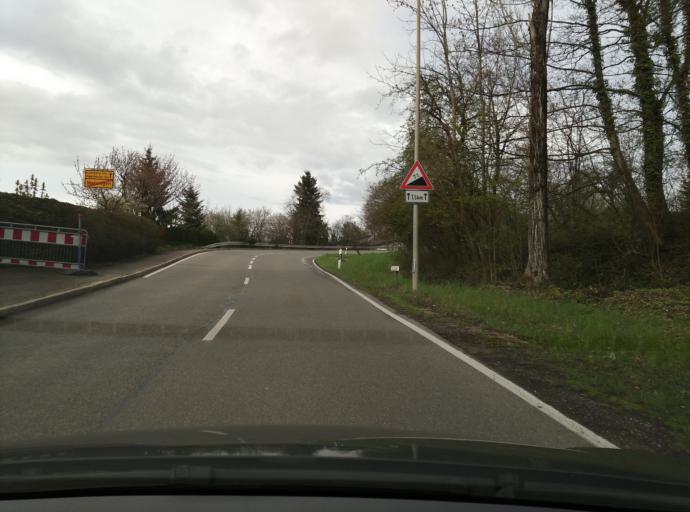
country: DE
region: Baden-Wuerttemberg
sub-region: Tuebingen Region
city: Metzingen
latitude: 48.5433
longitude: 9.2941
